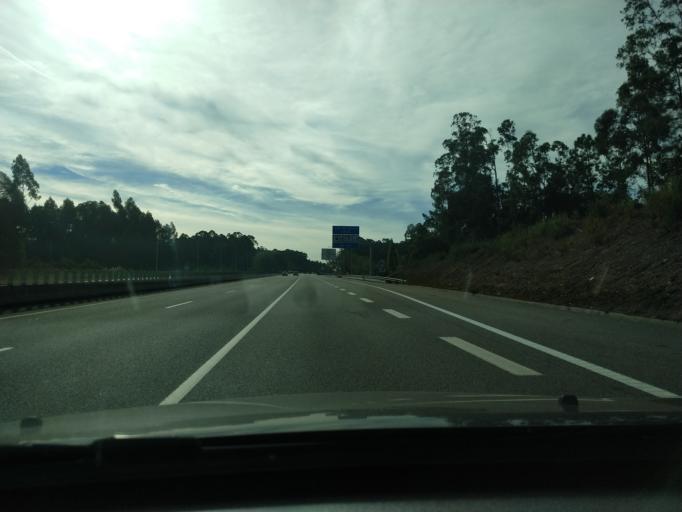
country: PT
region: Aveiro
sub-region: Santa Maria da Feira
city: Rio Meao
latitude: 40.9339
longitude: -8.5717
